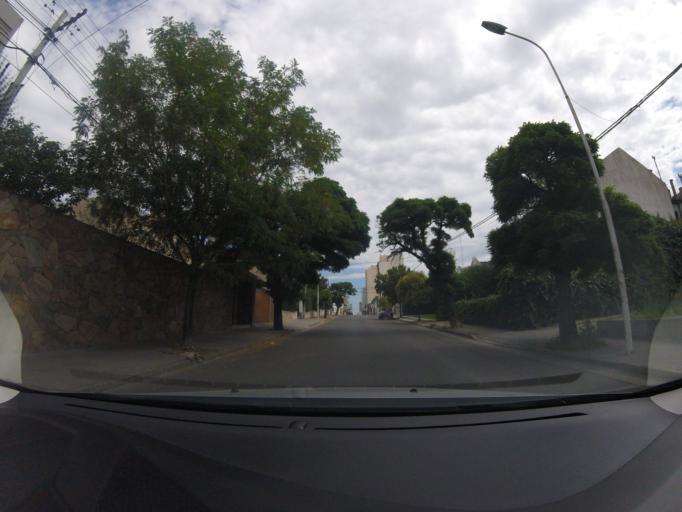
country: AR
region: Buenos Aires
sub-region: Partido de Tandil
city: Tandil
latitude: -37.3279
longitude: -59.1304
